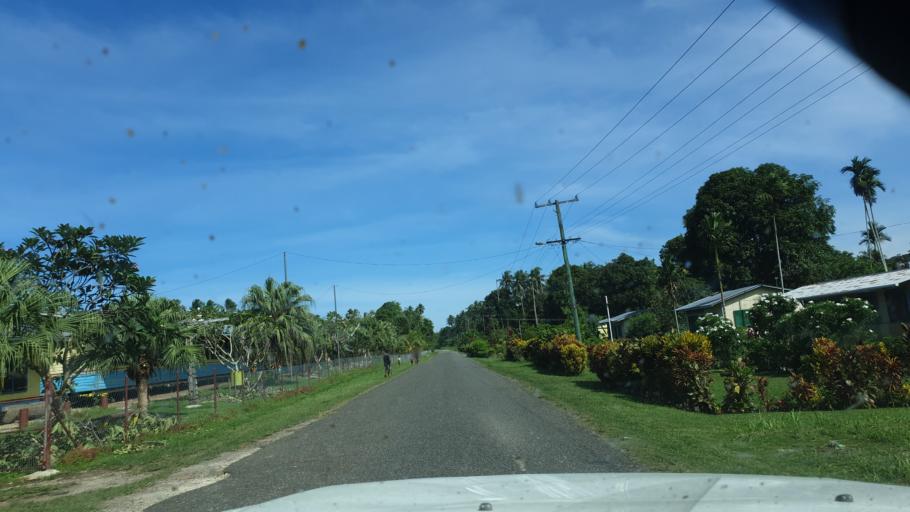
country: PG
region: Madang
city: Madang
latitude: -4.8134
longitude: 145.7621
